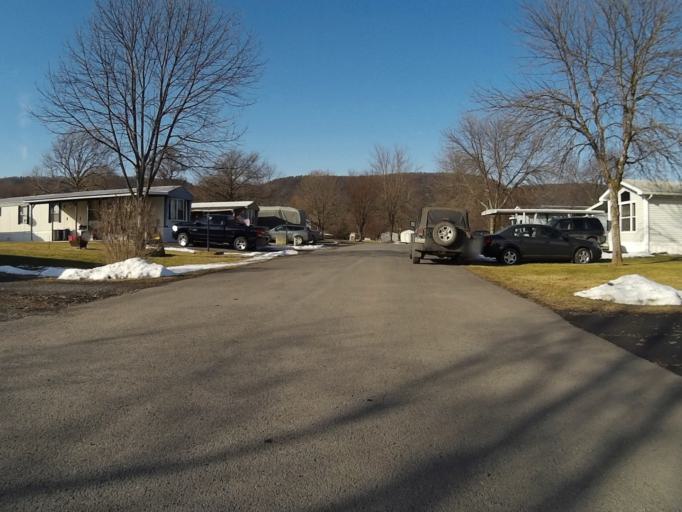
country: US
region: Pennsylvania
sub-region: Centre County
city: Houserville
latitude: 40.8710
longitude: -77.8628
